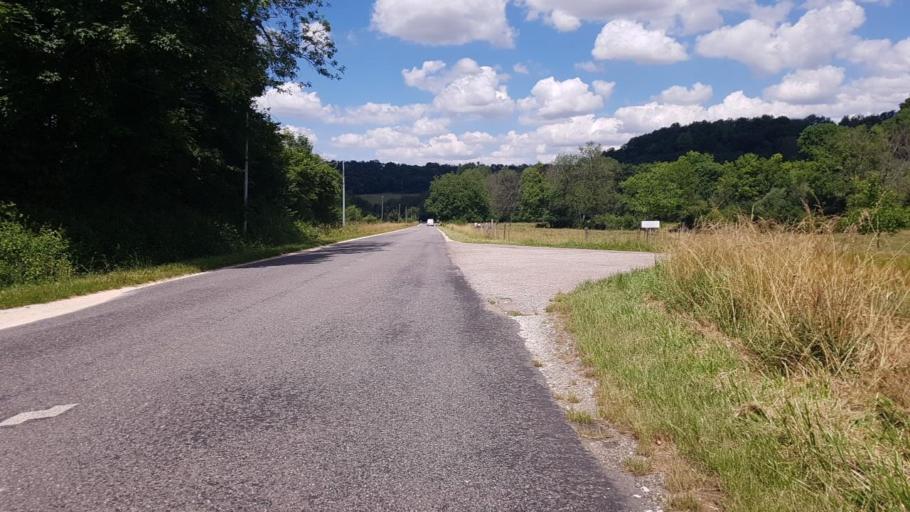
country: FR
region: Lorraine
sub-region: Departement de la Meuse
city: Ligny-en-Barrois
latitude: 48.6374
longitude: 5.4495
